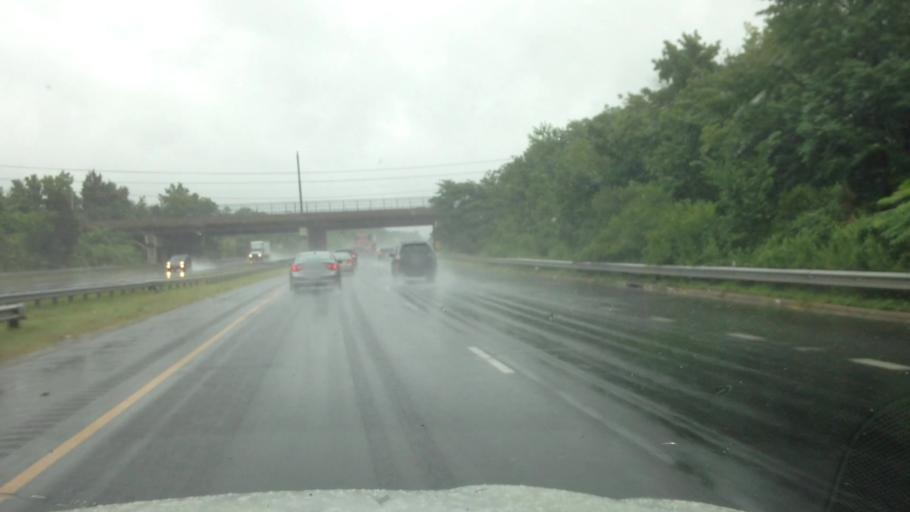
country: US
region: Maryland
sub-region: Prince George's County
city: Landover
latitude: 38.9295
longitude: -76.8990
